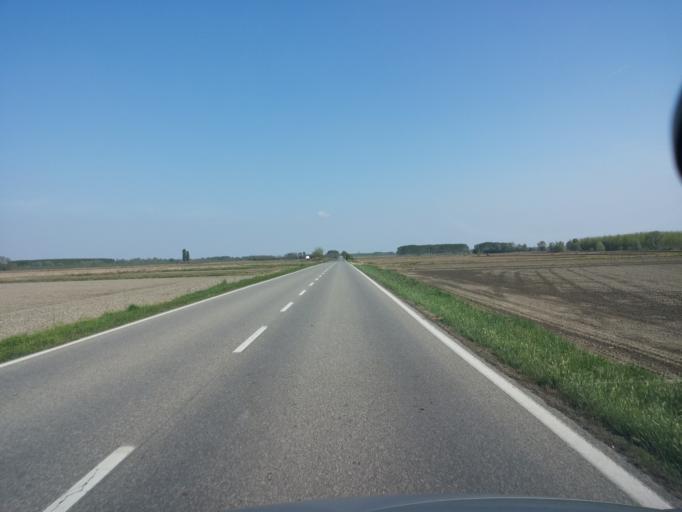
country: IT
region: Piedmont
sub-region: Provincia di Vercelli
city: Caresana
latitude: 45.2131
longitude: 8.5141
